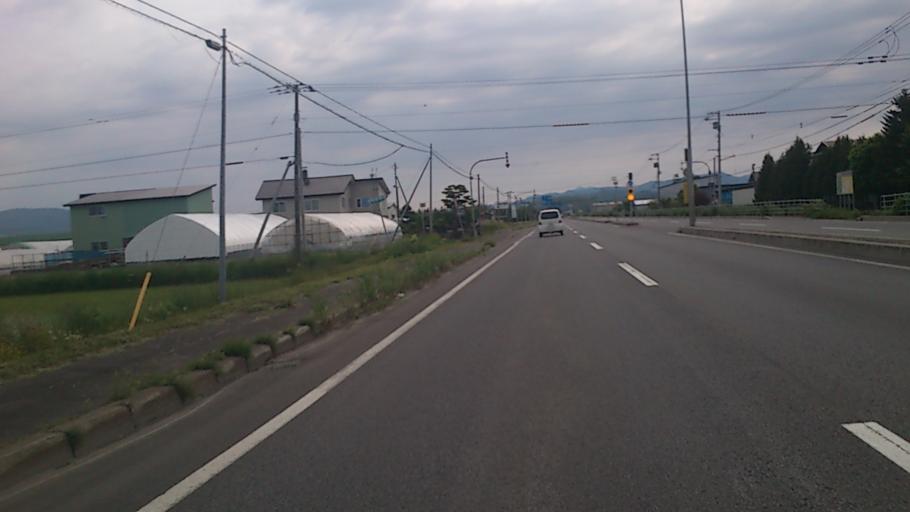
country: JP
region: Hokkaido
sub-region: Asahikawa-shi
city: Asahikawa
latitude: 43.8515
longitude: 142.4994
